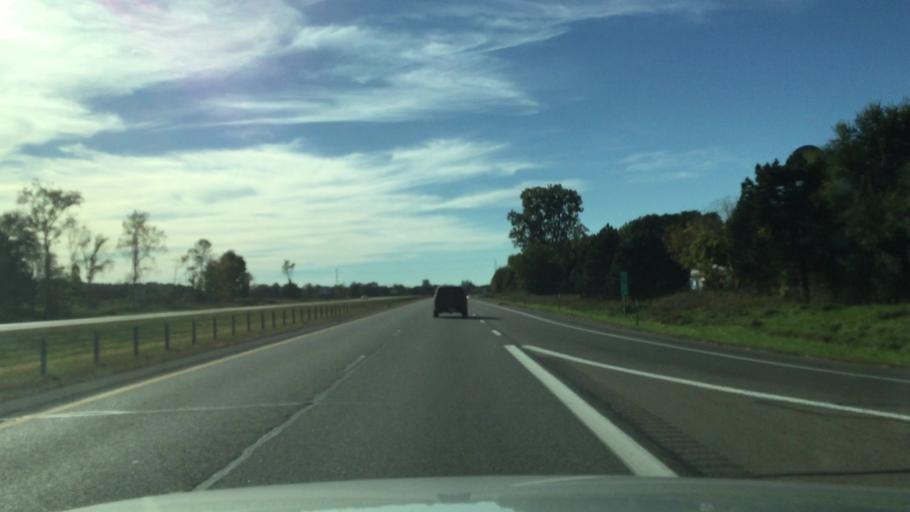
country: US
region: Michigan
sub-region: Calhoun County
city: Albion
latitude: 42.2643
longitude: -84.7599
